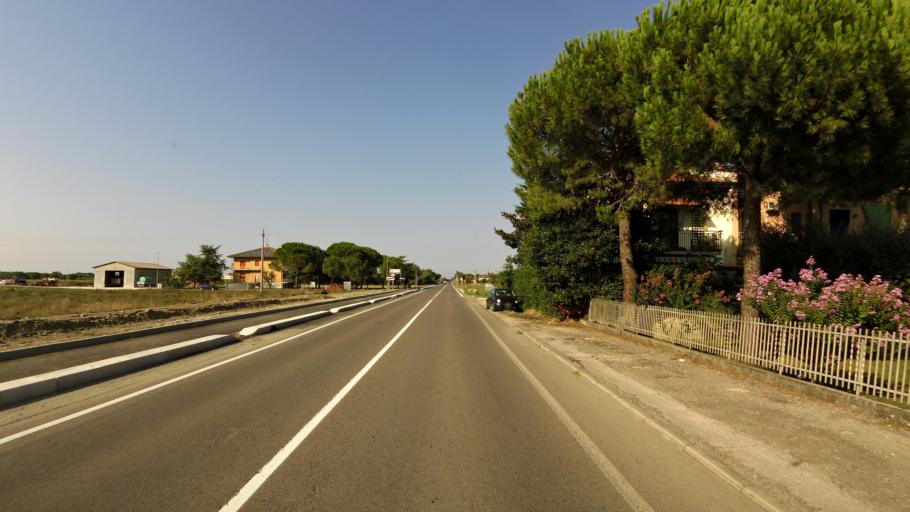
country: IT
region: Emilia-Romagna
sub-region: Provincia di Ravenna
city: Cervia
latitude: 44.2143
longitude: 12.3335
